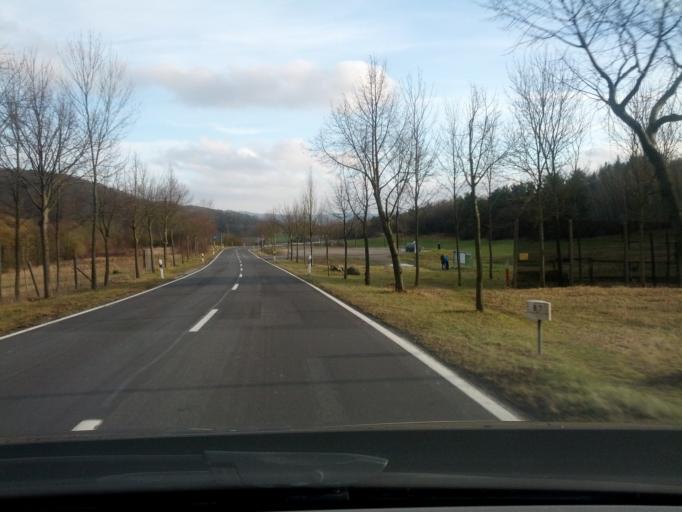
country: DE
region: Thuringia
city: Ifta
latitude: 51.0767
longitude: 10.1507
